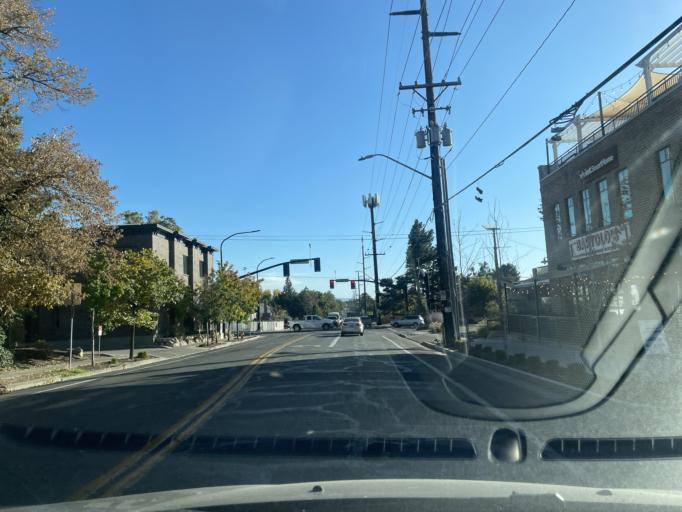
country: US
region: Utah
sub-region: Salt Lake County
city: Salt Lake City
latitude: 40.7422
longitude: -111.8597
